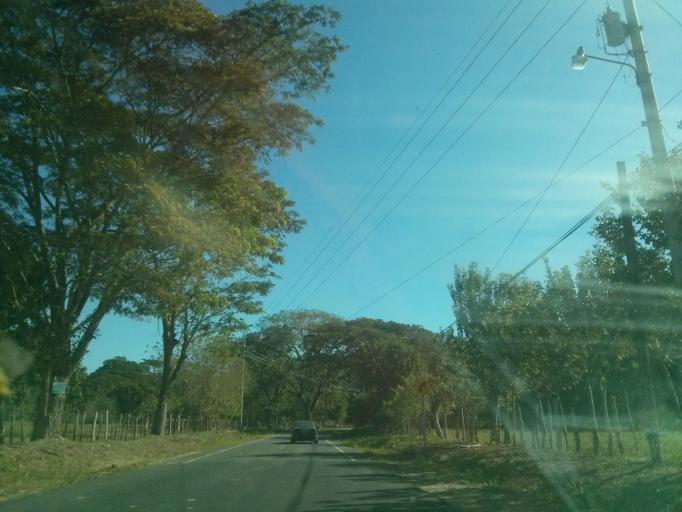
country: CR
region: Puntarenas
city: Paquera
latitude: 9.7556
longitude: -85.0005
